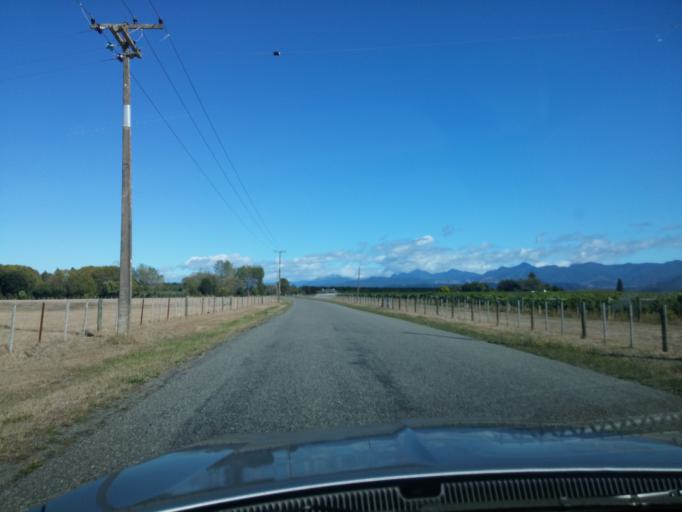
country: NZ
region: Marlborough
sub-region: Marlborough District
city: Blenheim
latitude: -41.5265
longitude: 173.8440
